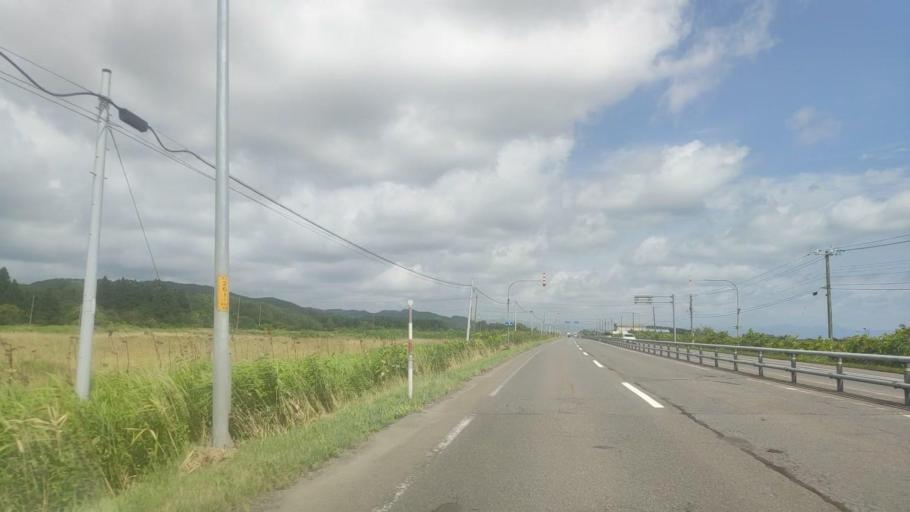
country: JP
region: Hokkaido
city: Niseko Town
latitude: 42.4112
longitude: 140.3072
